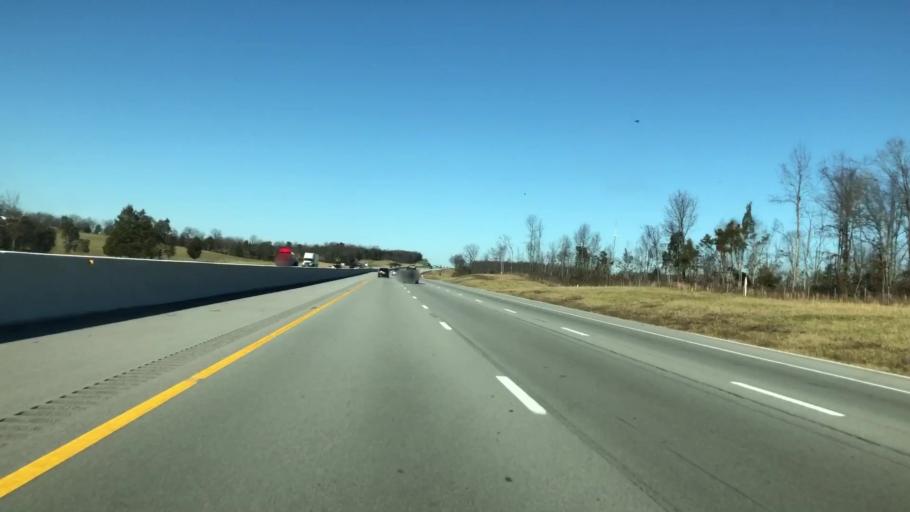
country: US
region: Kentucky
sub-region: Hart County
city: Munfordville
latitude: 37.4346
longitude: -85.8851
